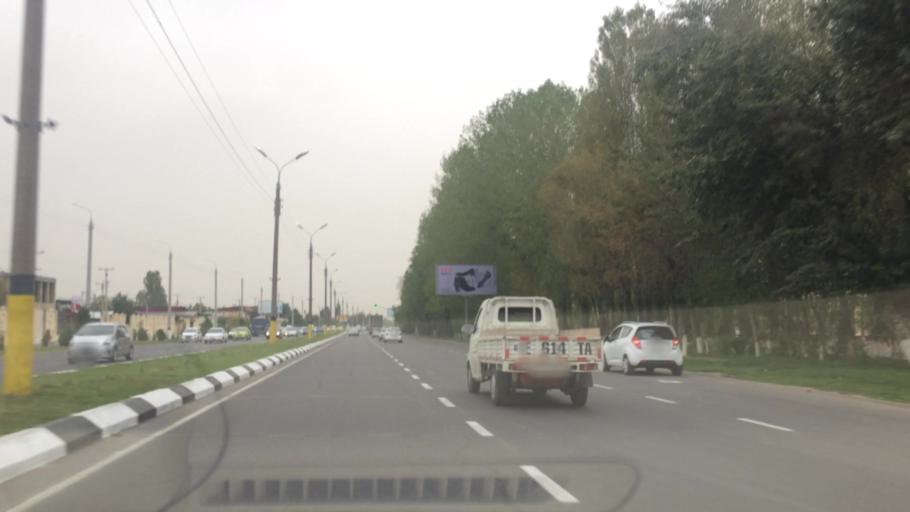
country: UZ
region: Toshkent
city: Salor
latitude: 41.3182
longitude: 69.3580
